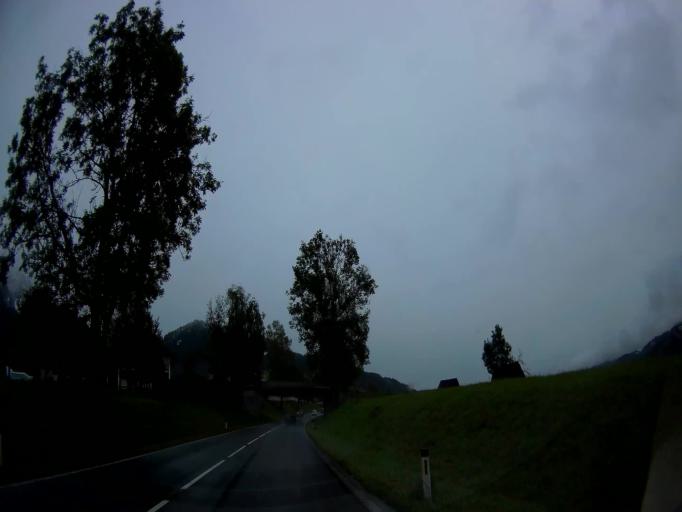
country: AT
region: Styria
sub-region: Politischer Bezirk Liezen
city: Aich
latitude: 47.4210
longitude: 13.8256
